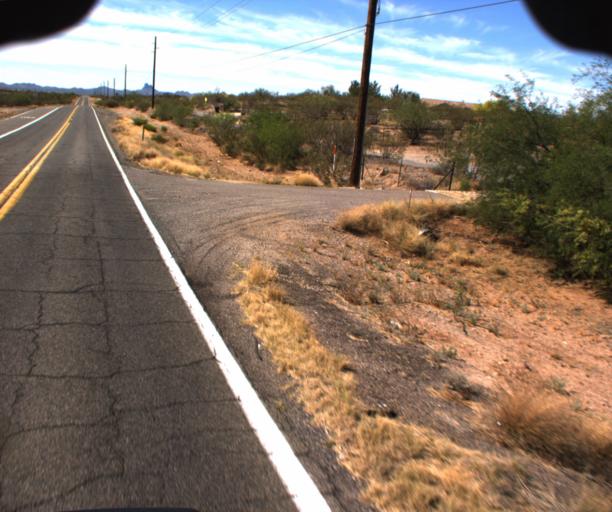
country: US
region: Arizona
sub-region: Maricopa County
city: Wickenburg
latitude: 34.0461
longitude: -112.8150
